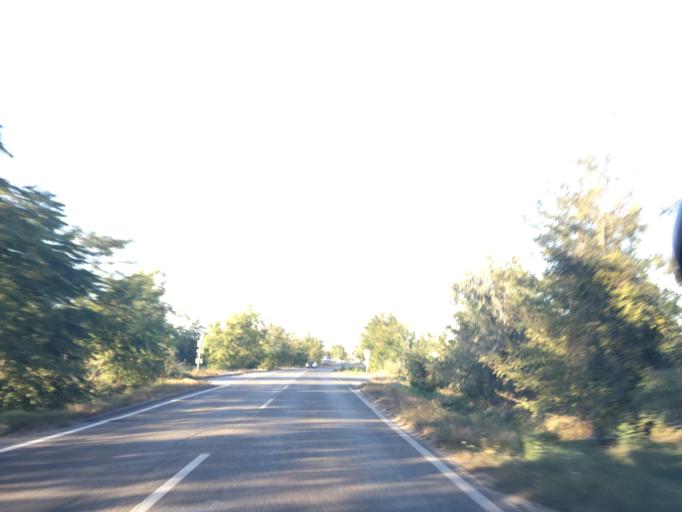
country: HU
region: Pest
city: Szazhalombatta
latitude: 47.3338
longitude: 18.8947
